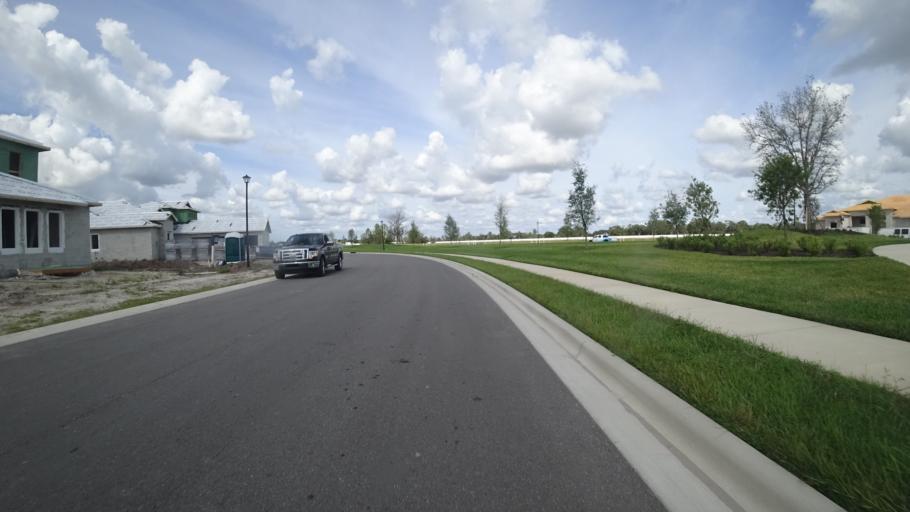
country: US
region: Florida
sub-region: Sarasota County
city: The Meadows
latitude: 27.3976
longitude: -82.3582
